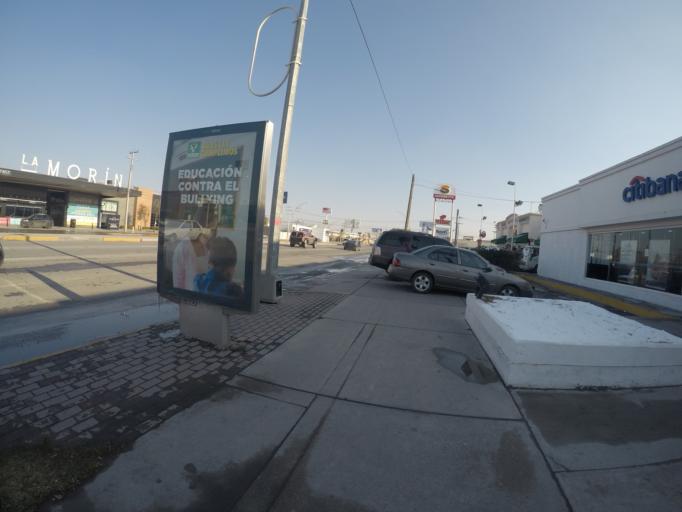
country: MX
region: Chihuahua
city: Ciudad Juarez
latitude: 31.7134
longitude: -106.4110
